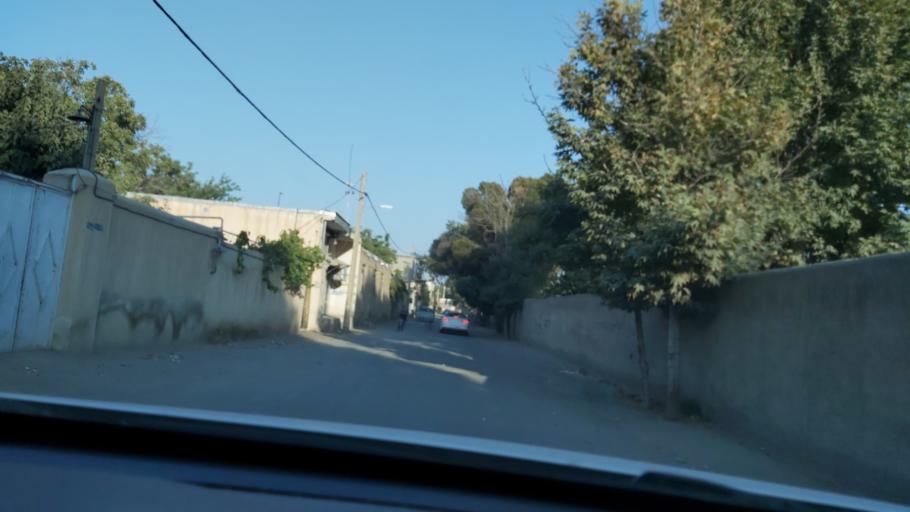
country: IR
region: Alborz
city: Hashtgerd
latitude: 35.8603
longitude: 50.6887
